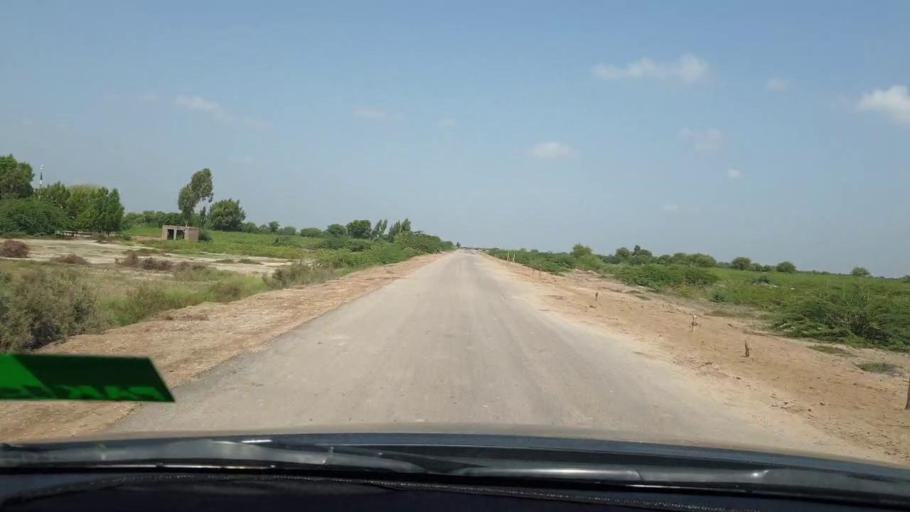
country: PK
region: Sindh
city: Digri
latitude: 24.9826
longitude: 69.1275
